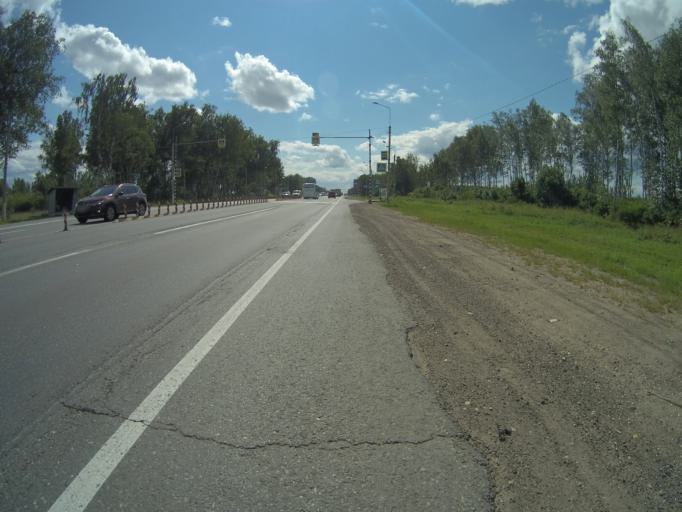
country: RU
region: Vladimir
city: Vorsha
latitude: 56.0745
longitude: 40.1746
